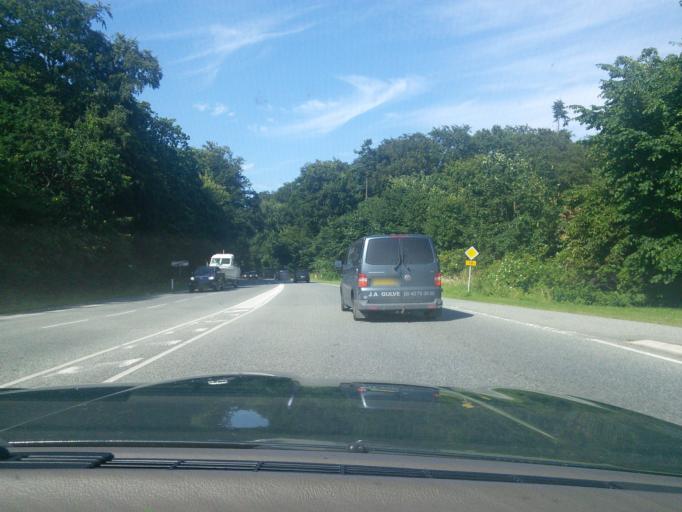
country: DK
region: Capital Region
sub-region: Halsnaes Kommune
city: Frederiksvaerk
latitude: 55.9701
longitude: 12.0303
